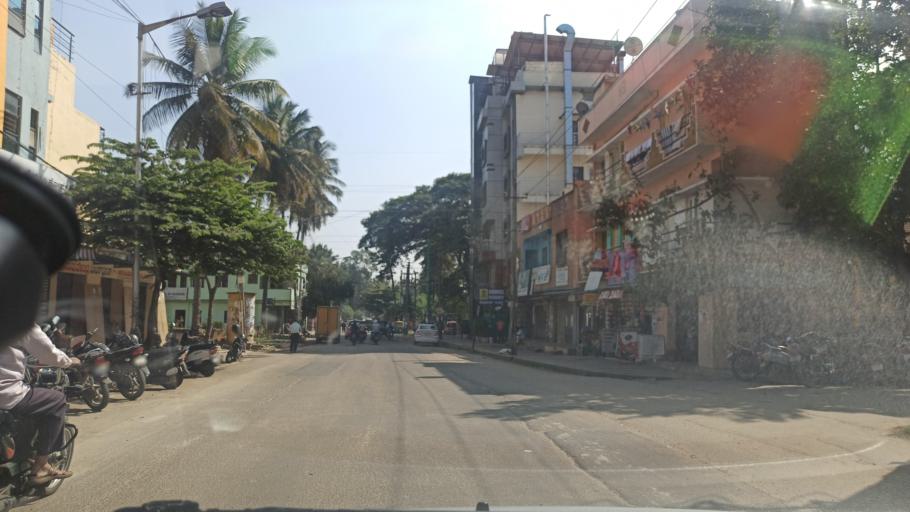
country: IN
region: Karnataka
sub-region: Bangalore Urban
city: Yelahanka
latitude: 13.0423
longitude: 77.5816
